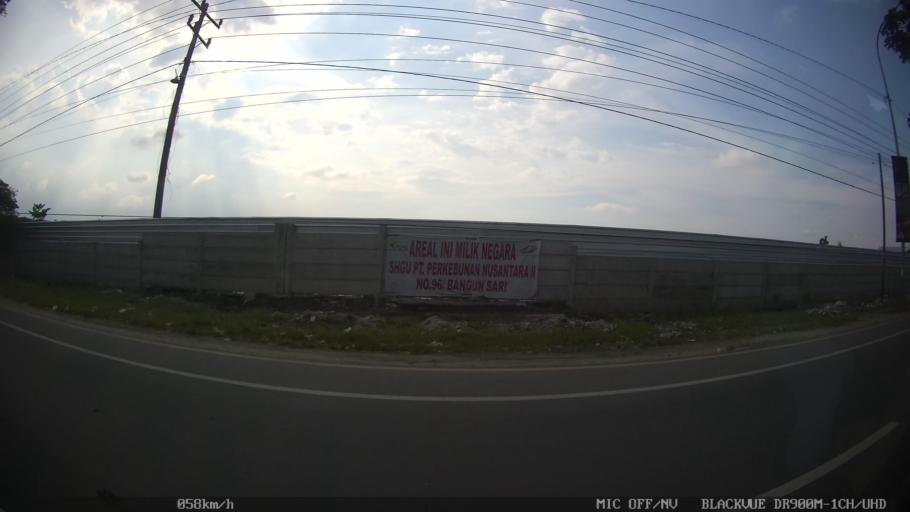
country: ID
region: North Sumatra
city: Percut
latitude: 3.5663
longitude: 98.7946
